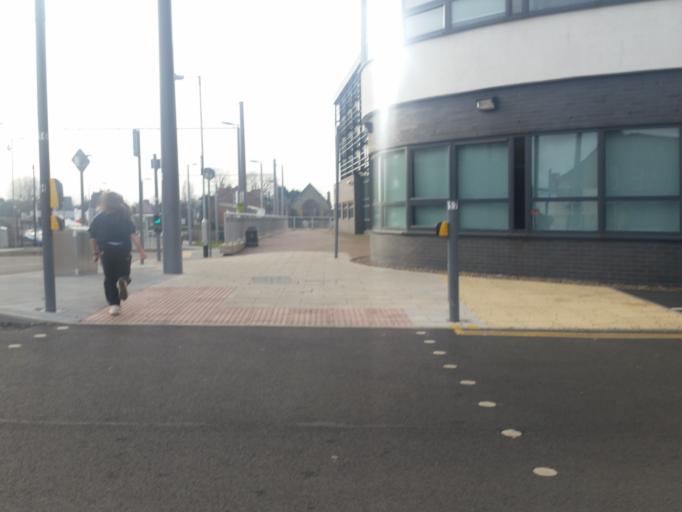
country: GB
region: England
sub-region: Derbyshire
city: Long Eaton
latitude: 52.9217
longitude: -1.2228
